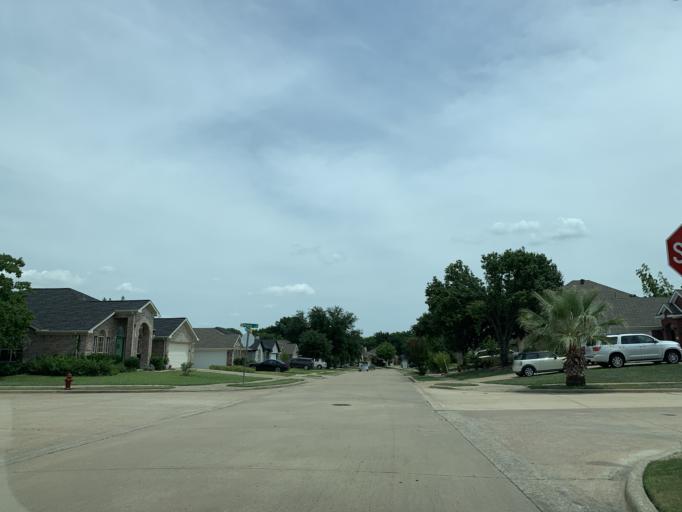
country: US
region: Texas
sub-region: Dallas County
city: Grand Prairie
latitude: 32.6612
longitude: -97.0211
